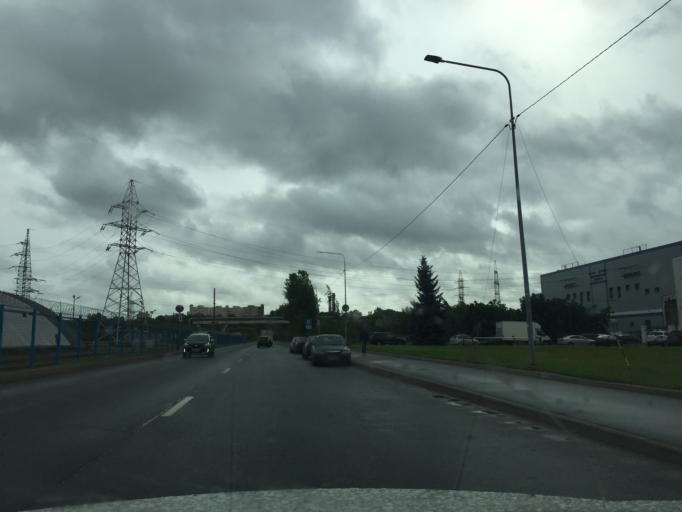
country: RU
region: St.-Petersburg
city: Sosnovaya Polyana
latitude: 59.8530
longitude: 30.1251
